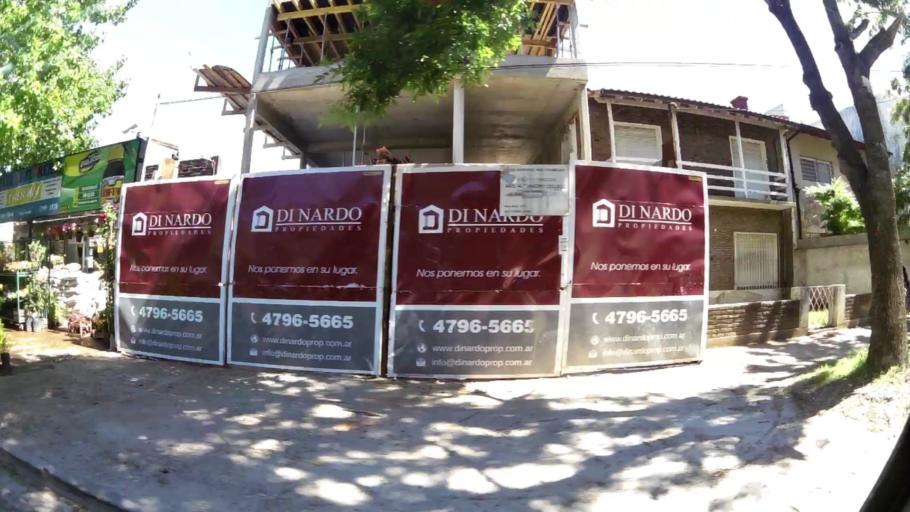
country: AR
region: Buenos Aires
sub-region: Partido de Vicente Lopez
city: Olivos
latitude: -34.5189
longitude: -58.5016
